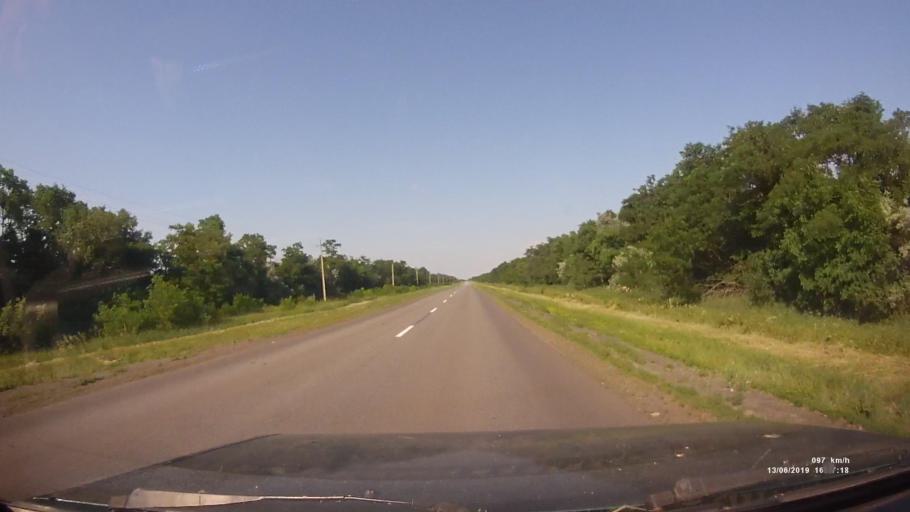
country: RU
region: Rostov
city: Kazanskaya
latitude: 49.8123
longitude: 41.1808
